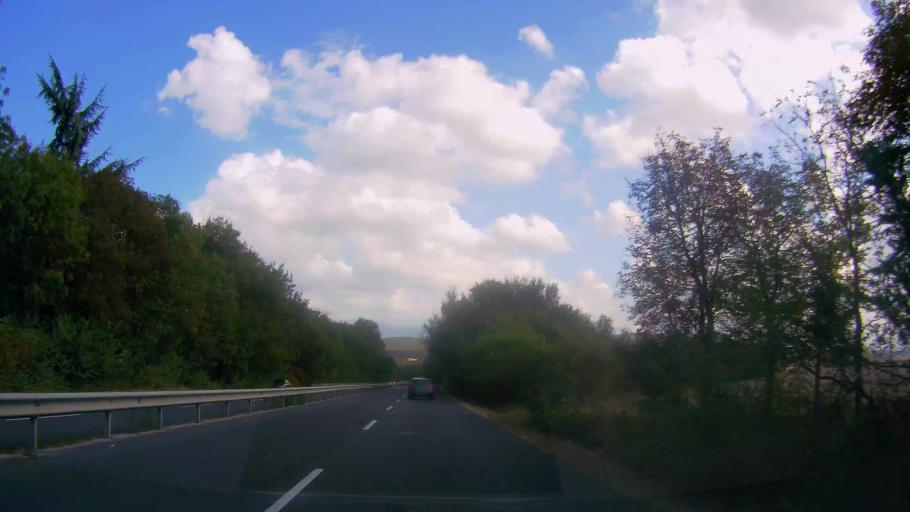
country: BG
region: Burgas
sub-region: Obshtina Burgas
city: Burgas
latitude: 42.4322
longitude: 27.4969
